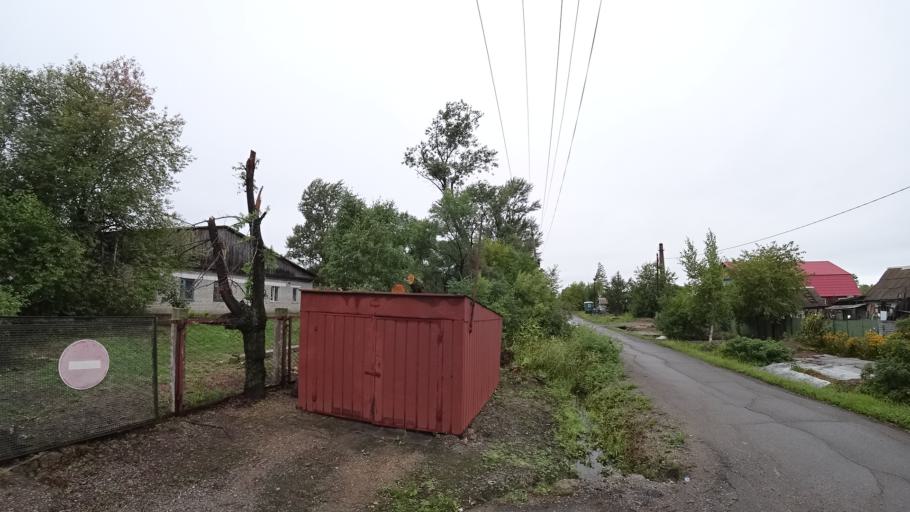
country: RU
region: Primorskiy
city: Monastyrishche
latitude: 44.2089
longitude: 132.4454
